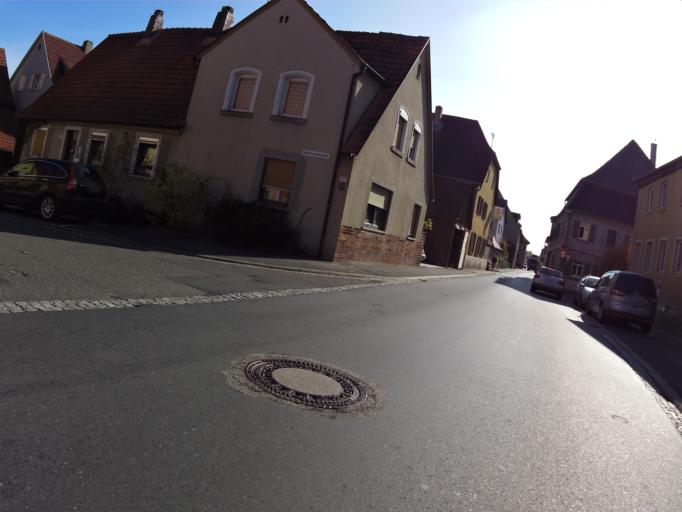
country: DE
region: Bavaria
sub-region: Regierungsbezirk Unterfranken
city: Winterhausen
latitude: 49.7060
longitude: 10.0159
